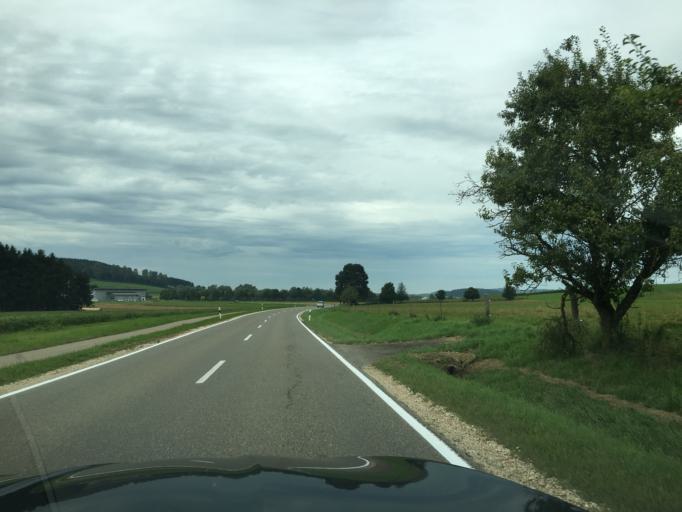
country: DE
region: Baden-Wuerttemberg
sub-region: Tuebingen Region
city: Rot
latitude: 47.8821
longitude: 9.1315
